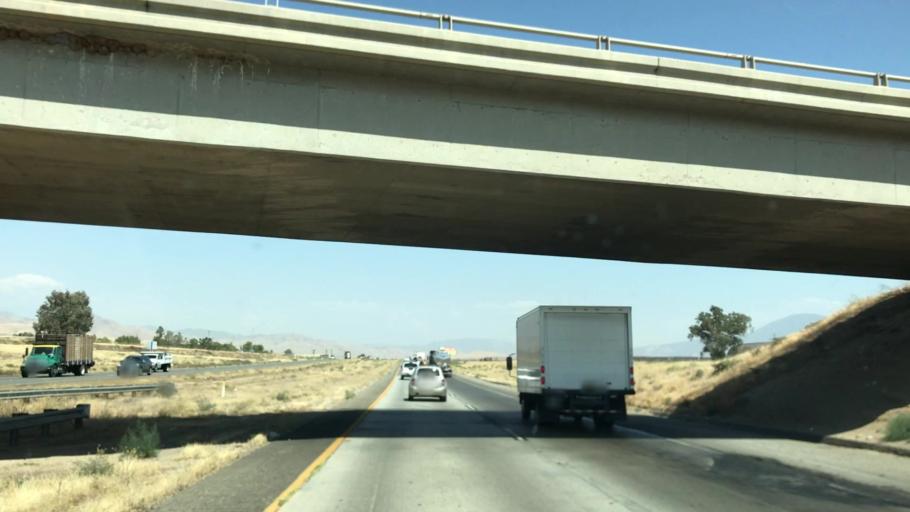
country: US
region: California
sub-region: Kern County
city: Lamont
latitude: 35.3455
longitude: -118.8789
